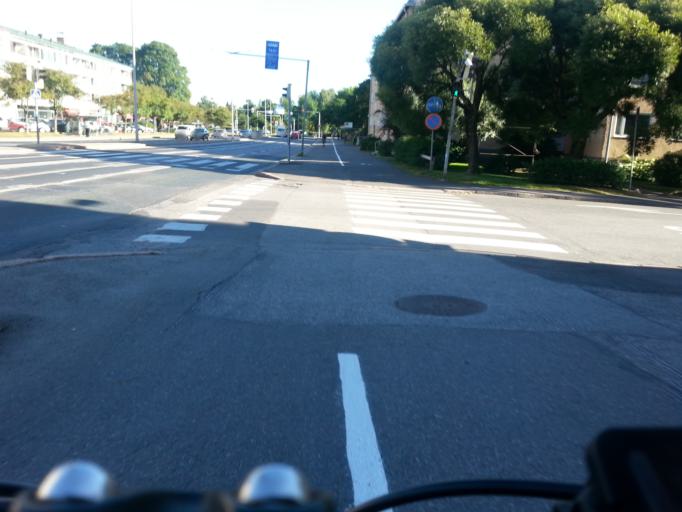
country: FI
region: Uusimaa
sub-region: Helsinki
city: Teekkarikylae
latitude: 60.2107
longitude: 24.8878
